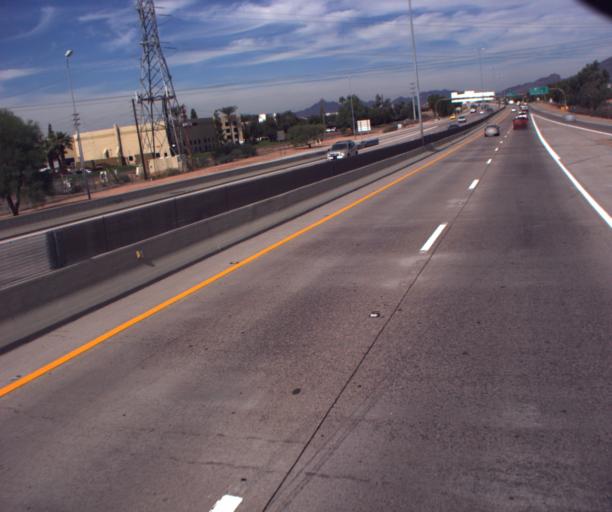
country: US
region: Arizona
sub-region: Maricopa County
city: Tempe Junction
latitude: 33.4248
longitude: -111.9780
